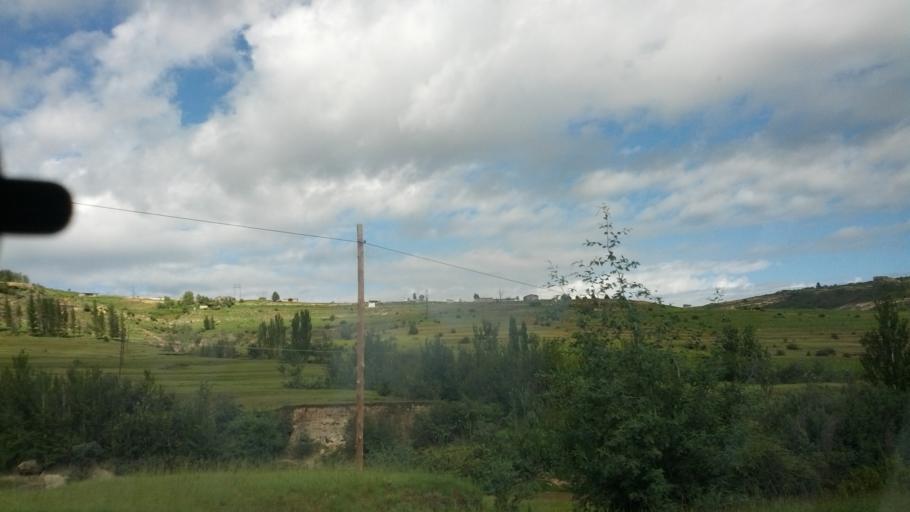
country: LS
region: Berea
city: Teyateyaneng
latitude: -29.1410
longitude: 27.7121
